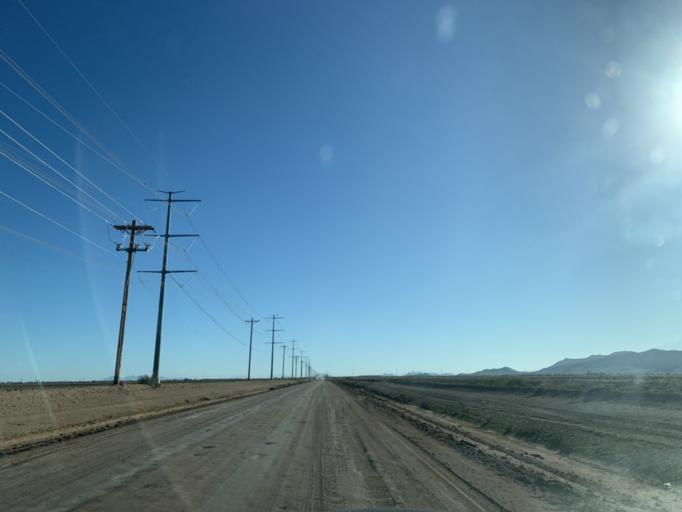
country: US
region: Arizona
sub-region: Pinal County
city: Casa Grande
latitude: 32.8637
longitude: -111.6709
